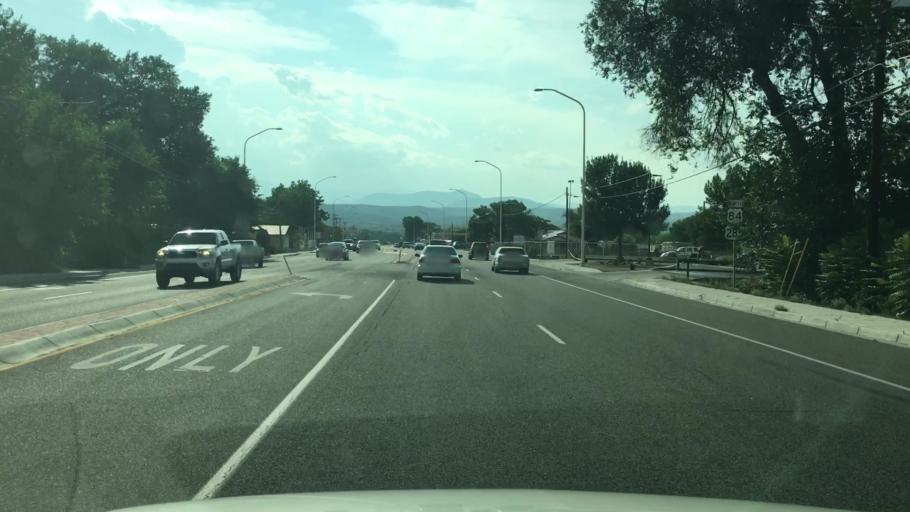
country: US
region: New Mexico
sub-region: Rio Arriba County
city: Espanola
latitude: 35.9873
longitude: -106.0596
